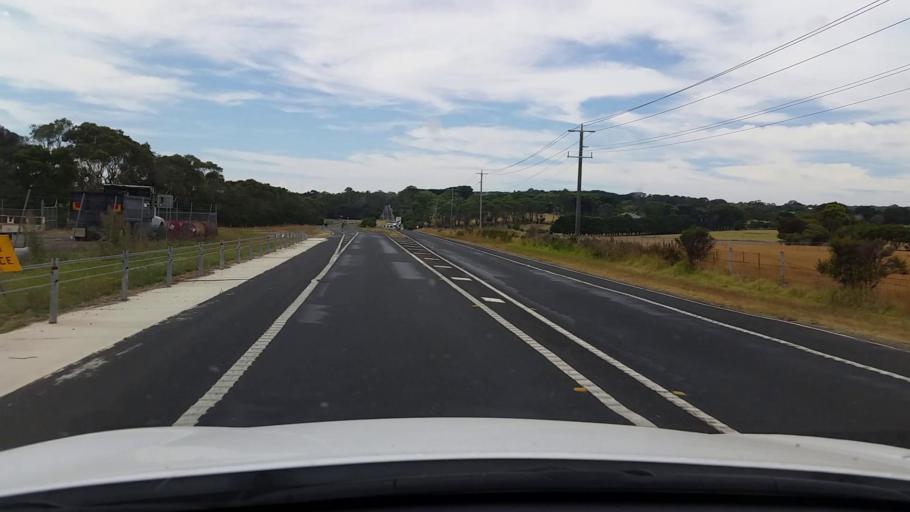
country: AU
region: Victoria
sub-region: Mornington Peninsula
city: Safety Beach
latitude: -38.3126
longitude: 145.0245
